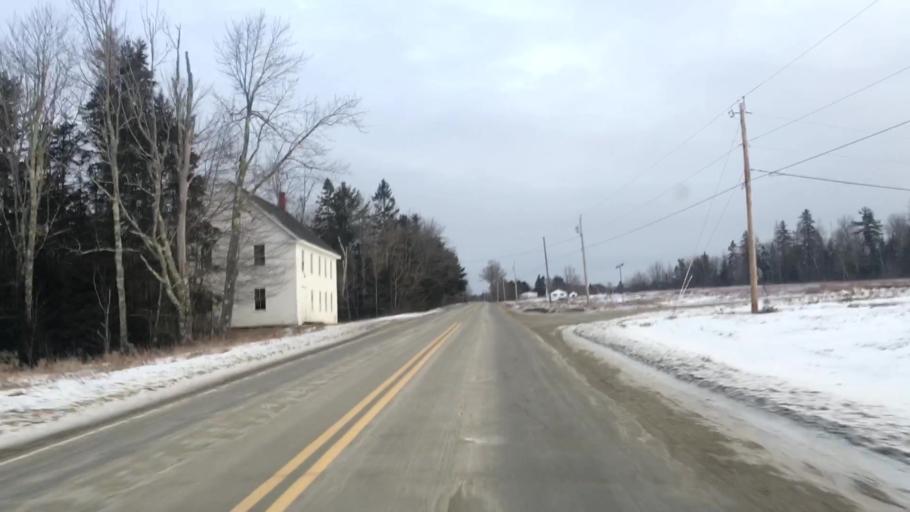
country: US
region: Maine
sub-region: Hancock County
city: Franklin
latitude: 44.7115
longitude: -68.3384
